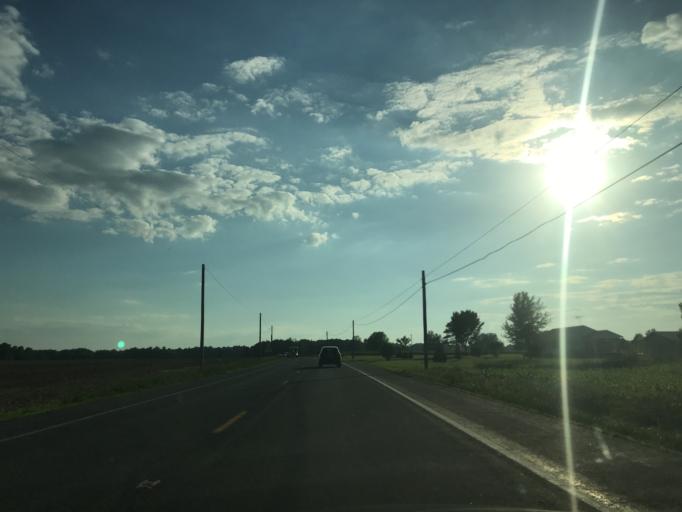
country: US
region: Maryland
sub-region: Talbot County
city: Easton
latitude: 38.8162
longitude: -75.9564
